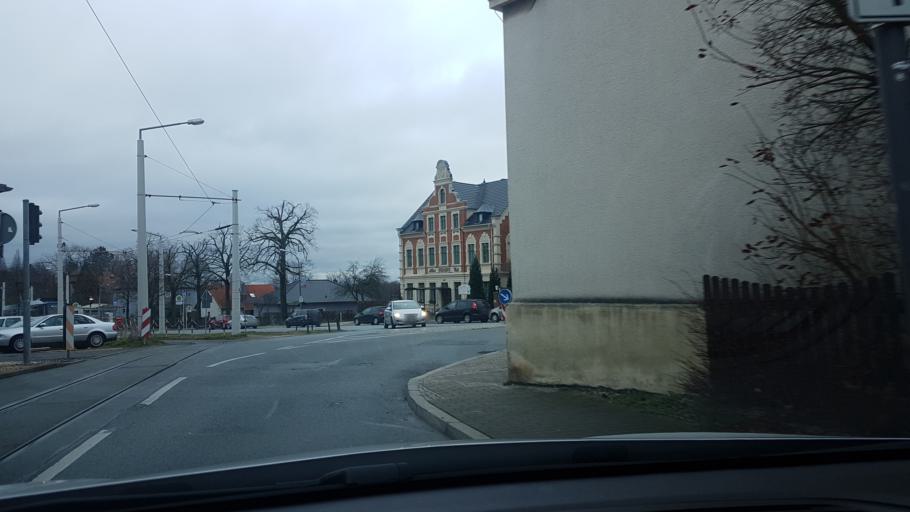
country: DE
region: Saxony
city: Goerlitz
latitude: 51.1326
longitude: 14.9407
